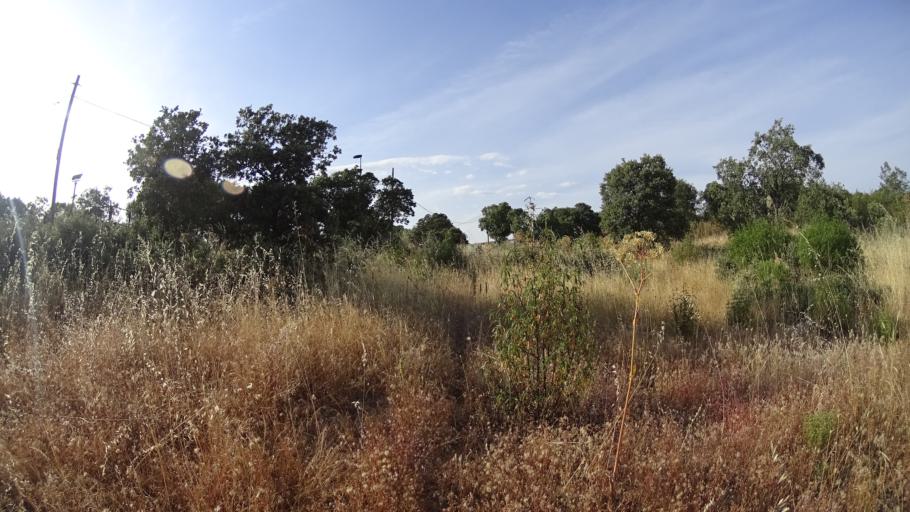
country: ES
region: Madrid
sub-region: Provincia de Madrid
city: Torrelodones
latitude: 40.5893
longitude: -3.9434
